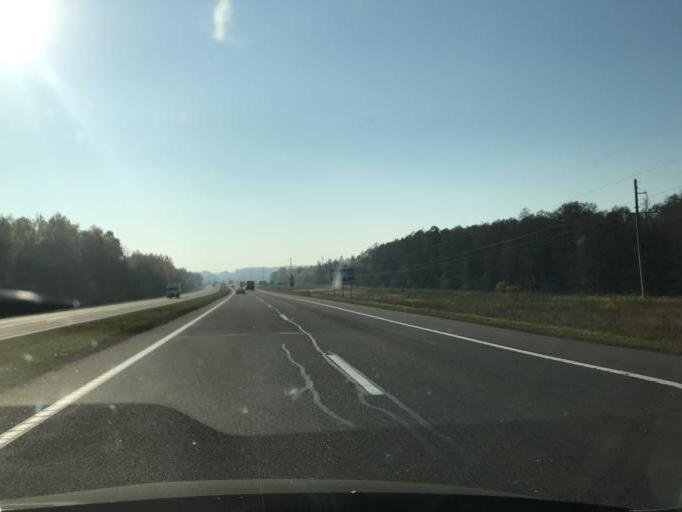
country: BY
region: Minsk
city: Stowbtsy
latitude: 53.5104
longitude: 26.6724
